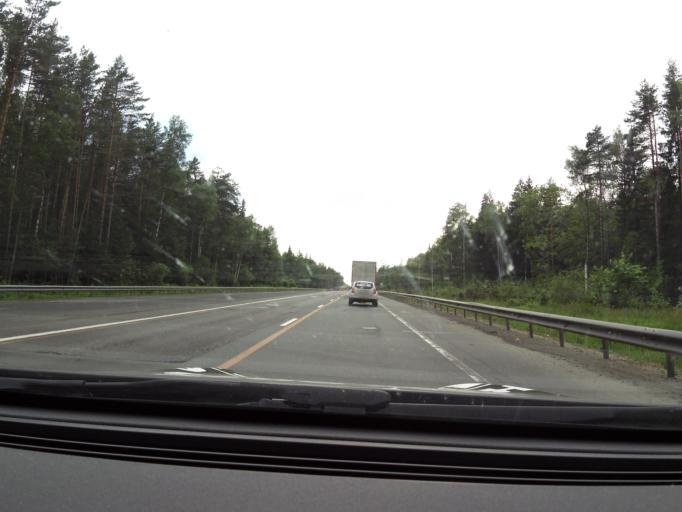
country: RU
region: Vladimir
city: Nikologory
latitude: 56.2358
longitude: 41.9063
